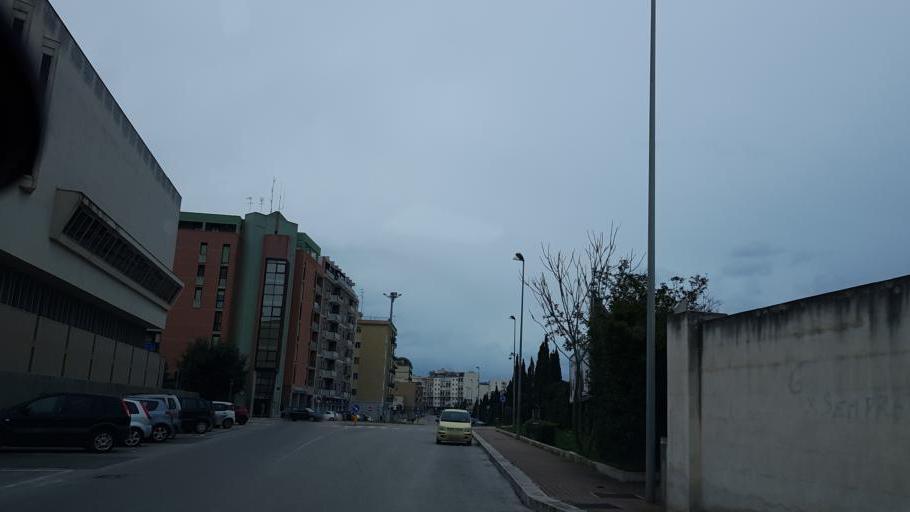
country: IT
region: Apulia
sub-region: Provincia di Brindisi
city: Brindisi
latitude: 40.6321
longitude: 17.9395
